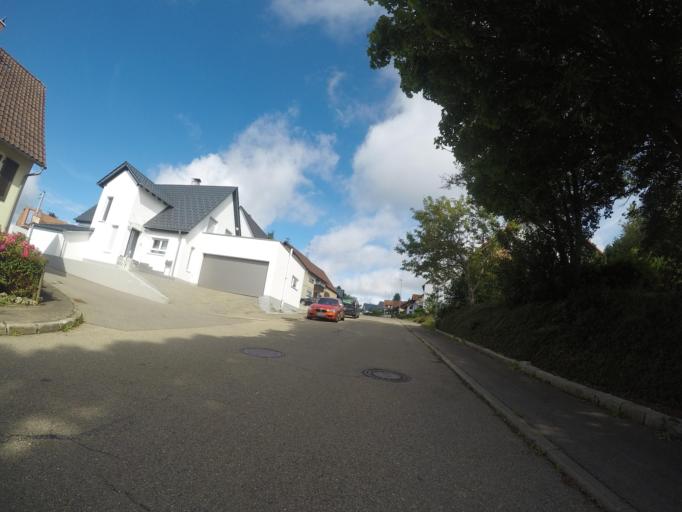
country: DE
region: Baden-Wuerttemberg
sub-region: Tuebingen Region
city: Laichingen
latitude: 48.4431
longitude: 9.6481
